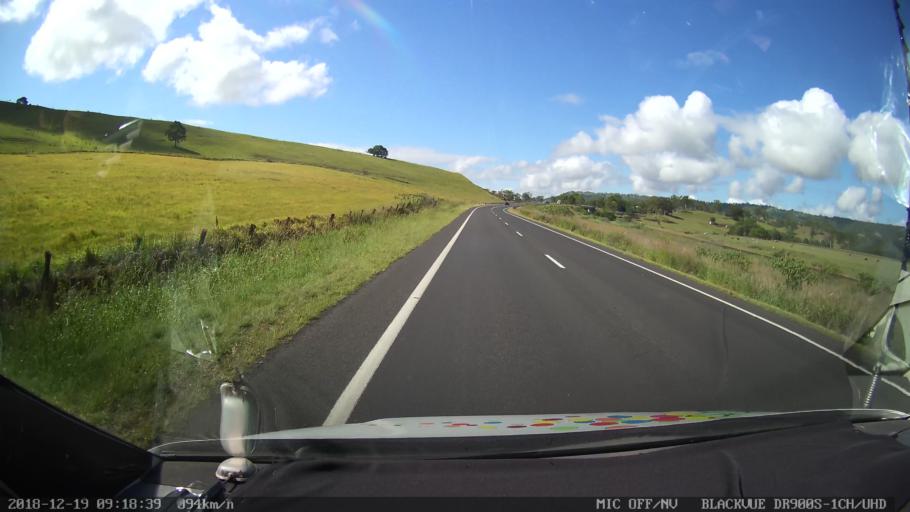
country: AU
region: New South Wales
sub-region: Kyogle
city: Kyogle
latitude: -28.5502
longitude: 152.9769
